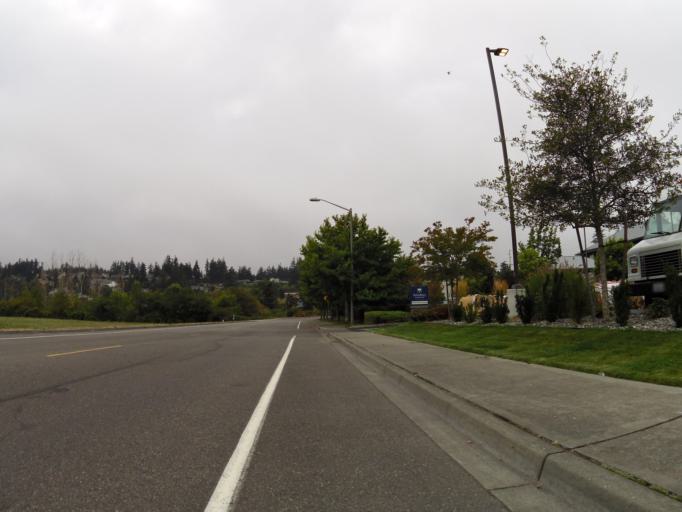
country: US
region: Washington
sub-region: Island County
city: Oak Harbor
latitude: 48.2848
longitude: -122.6611
